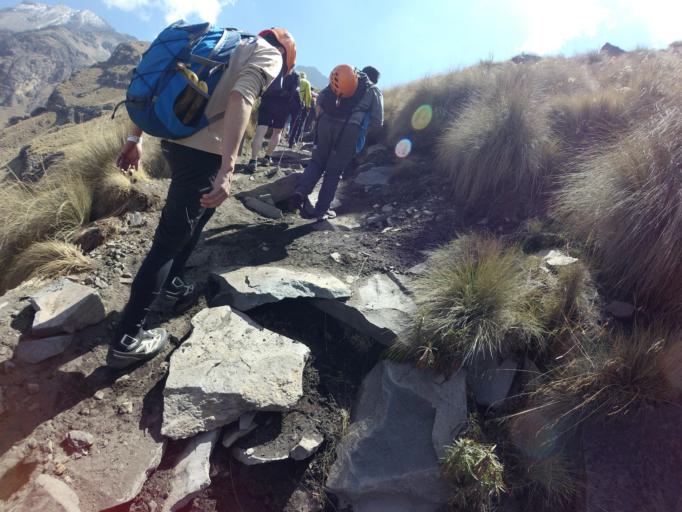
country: MX
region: Mexico
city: Amecameca de Juarez
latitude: 19.1392
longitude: -98.6447
